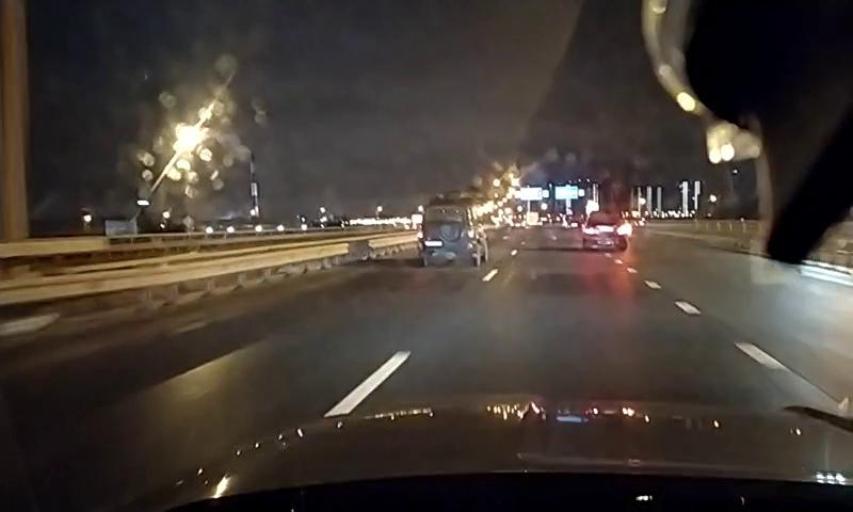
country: RU
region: Leningrad
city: Parnas
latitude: 60.0921
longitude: 30.3689
